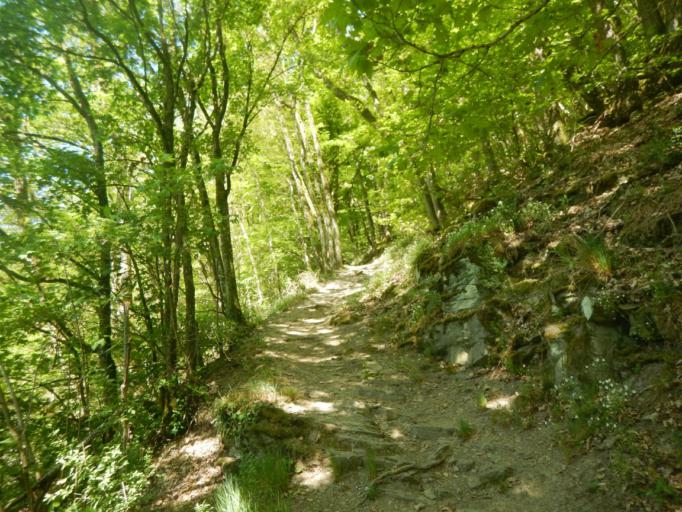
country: LU
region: Diekirch
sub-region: Canton de Diekirch
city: Bourscheid
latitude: 49.9147
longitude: 6.0875
